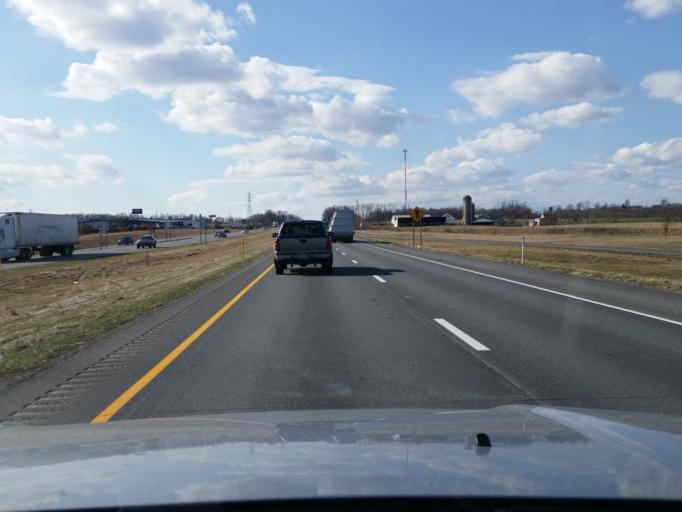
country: US
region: Pennsylvania
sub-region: Lancaster County
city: Rheems
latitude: 40.1445
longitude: -76.5568
